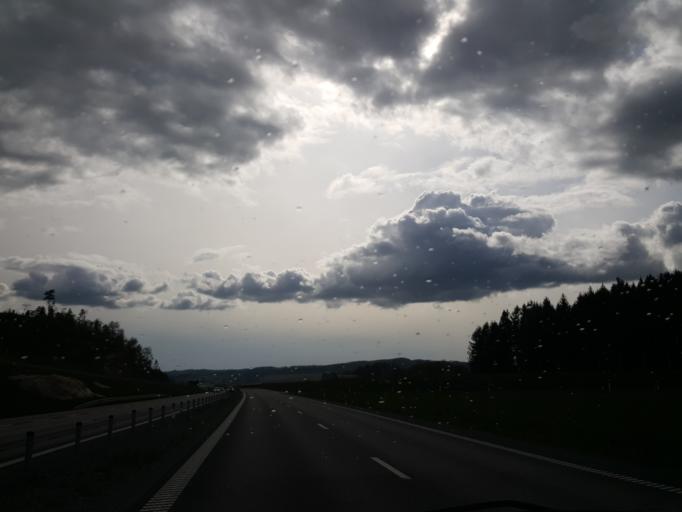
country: SE
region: Vaestra Goetaland
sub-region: Trollhattan
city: Sjuntorp
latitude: 58.2095
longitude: 12.1765
